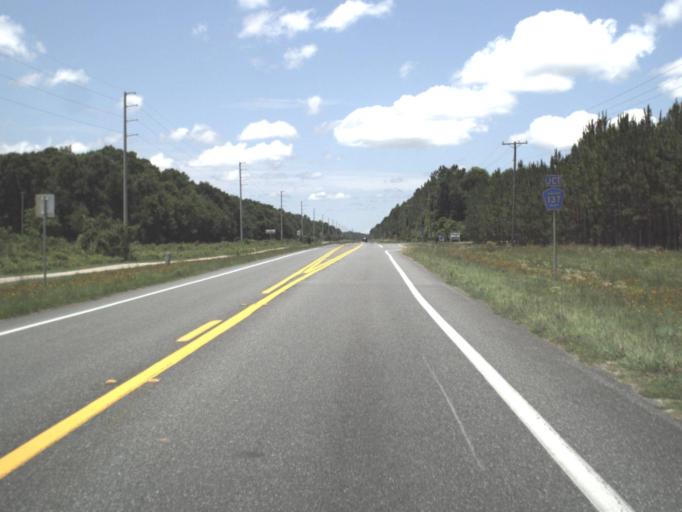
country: US
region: Florida
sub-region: Alachua County
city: High Springs
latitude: 29.9530
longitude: -82.8077
